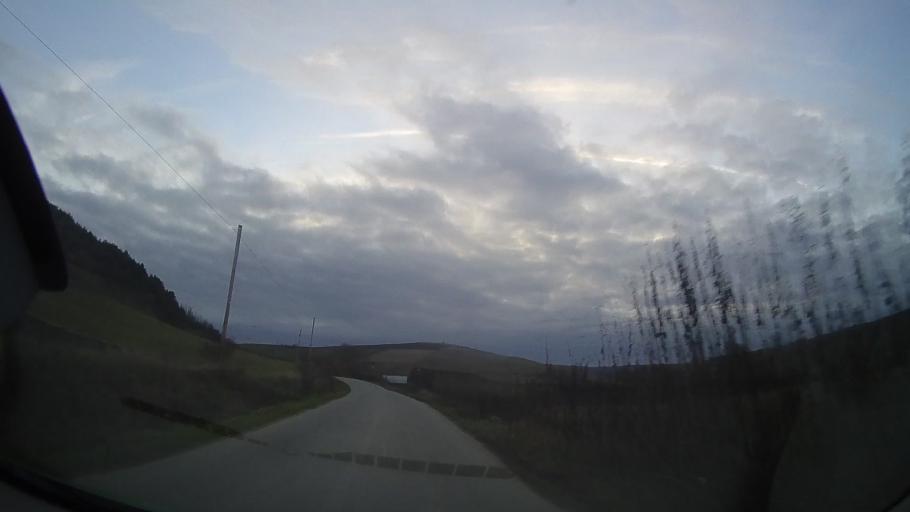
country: RO
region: Cluj
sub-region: Comuna Palatca
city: Palatca
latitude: 46.8645
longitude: 24.0041
